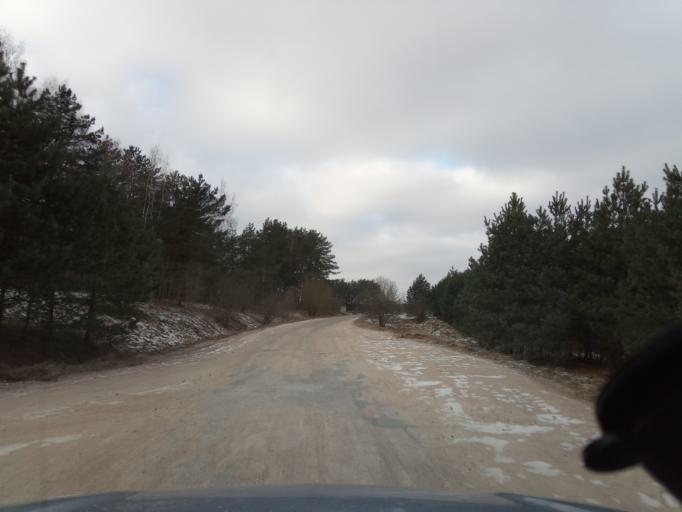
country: LT
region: Alytaus apskritis
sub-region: Alytaus rajonas
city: Daugai
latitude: 54.3279
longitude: 24.3006
